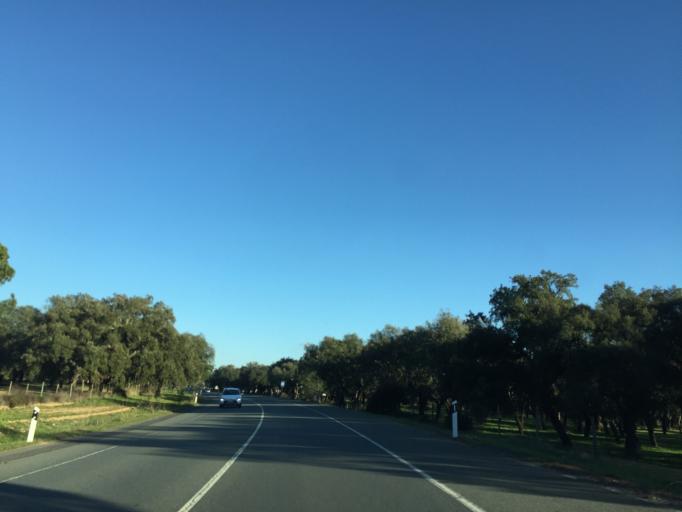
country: PT
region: Setubal
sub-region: Grandola
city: Grandola
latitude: 38.1225
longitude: -8.4521
